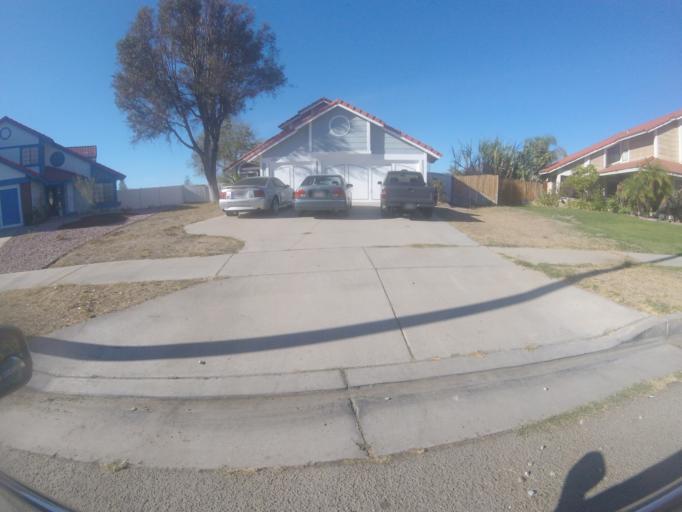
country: US
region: California
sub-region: San Bernardino County
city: Redlands
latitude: 34.0797
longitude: -117.1666
